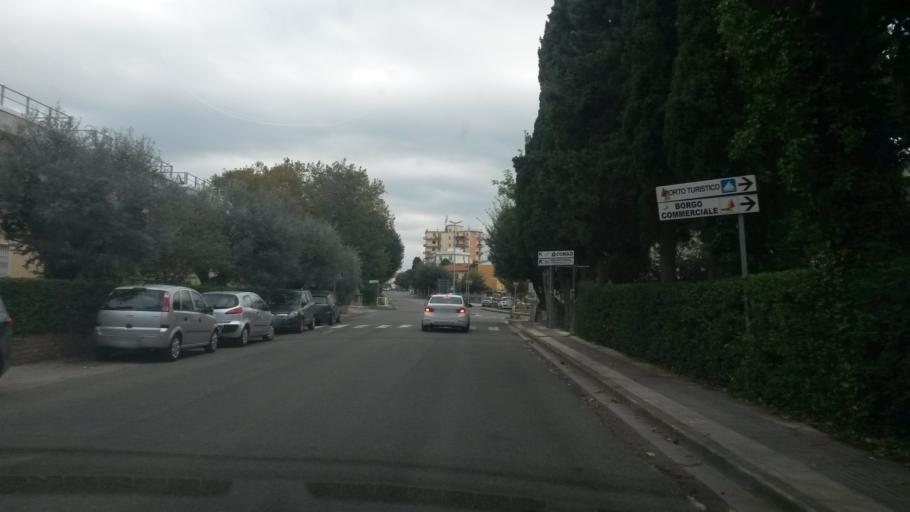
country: IT
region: Tuscany
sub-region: Provincia di Livorno
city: Rosignano Solvay-Castiglioncello
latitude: 43.3990
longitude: 10.4414
